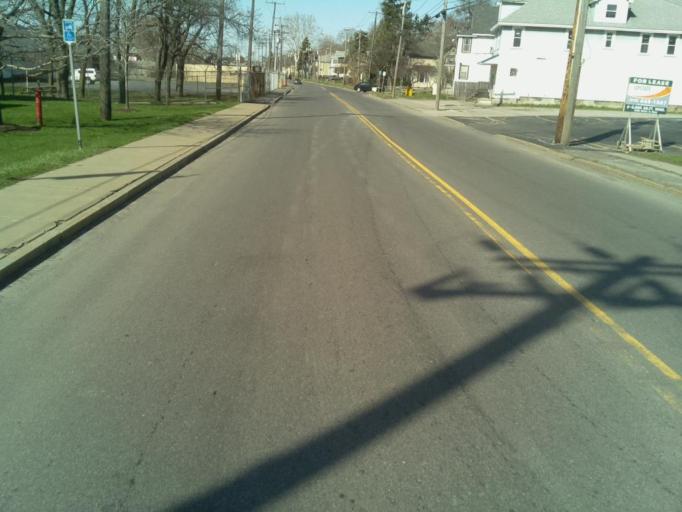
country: US
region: New York
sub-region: Onondaga County
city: Lyncourt
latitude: 43.0567
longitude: -76.1118
